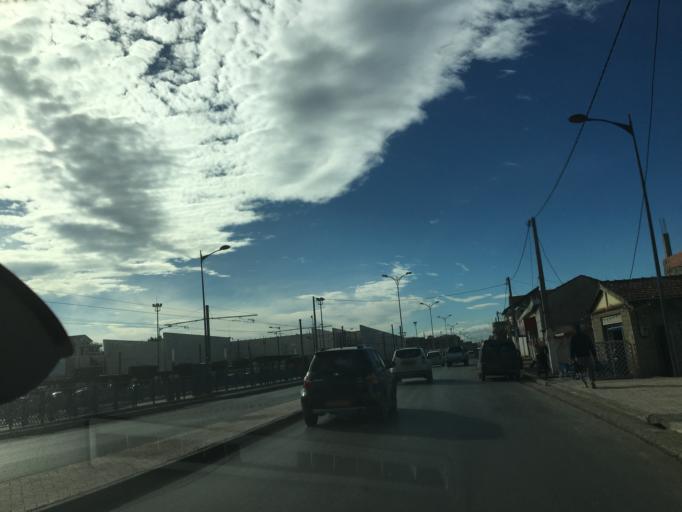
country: DZ
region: Alger
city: Bordj el Kiffan
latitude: 36.7507
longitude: 3.2127
